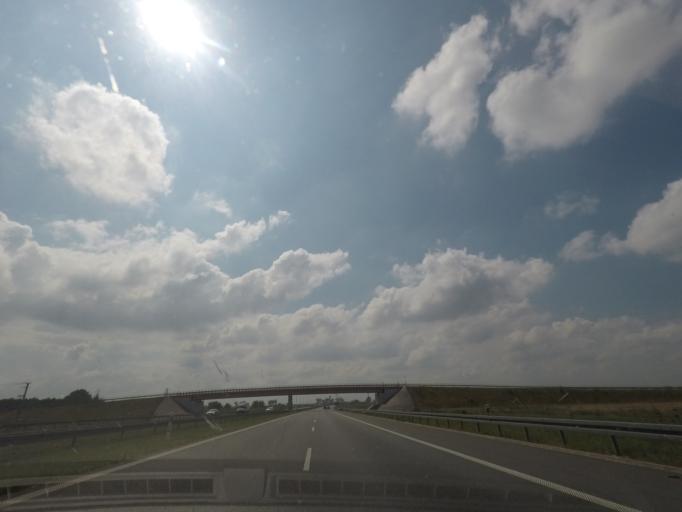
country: PL
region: Lodz Voivodeship
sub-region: Powiat kutnowski
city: Krzyzanow
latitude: 52.1935
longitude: 19.4867
